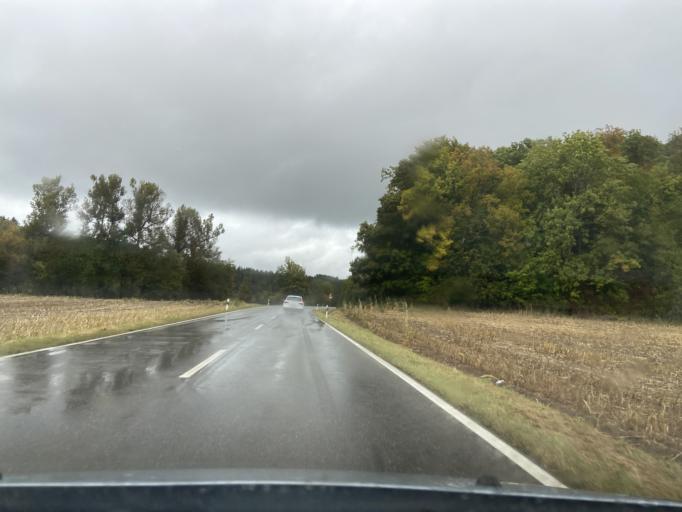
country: DE
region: Baden-Wuerttemberg
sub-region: Tuebingen Region
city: Bingen
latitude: 48.0913
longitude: 9.2812
